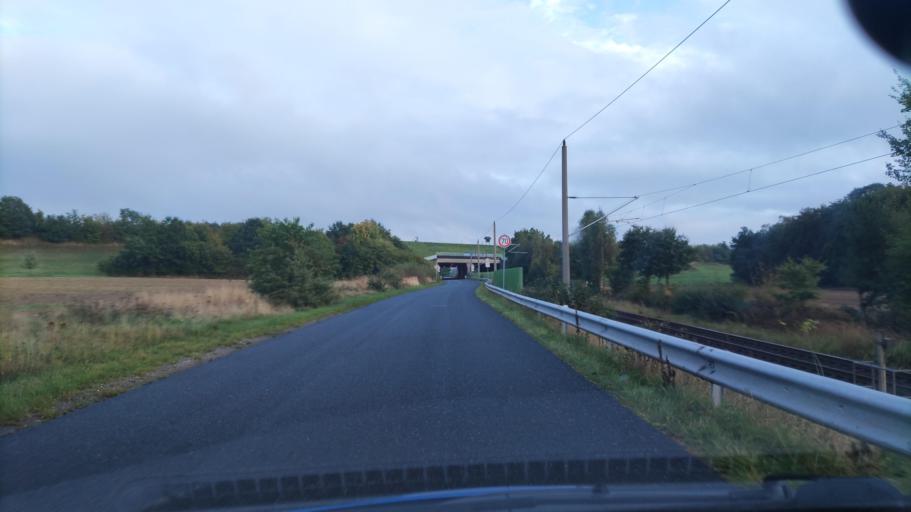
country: DE
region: Lower Saxony
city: Wrestedt
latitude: 52.9001
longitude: 10.6161
